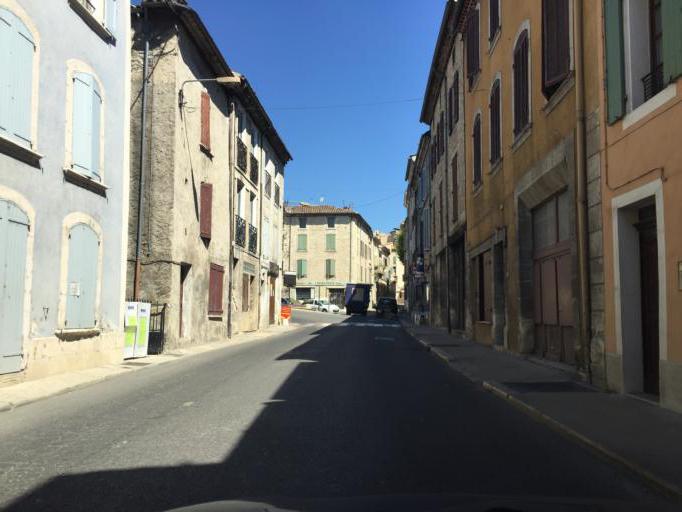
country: FR
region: Provence-Alpes-Cote d'Azur
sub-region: Departement des Alpes-de-Haute-Provence
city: Mane
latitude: 43.9368
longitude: 5.7657
